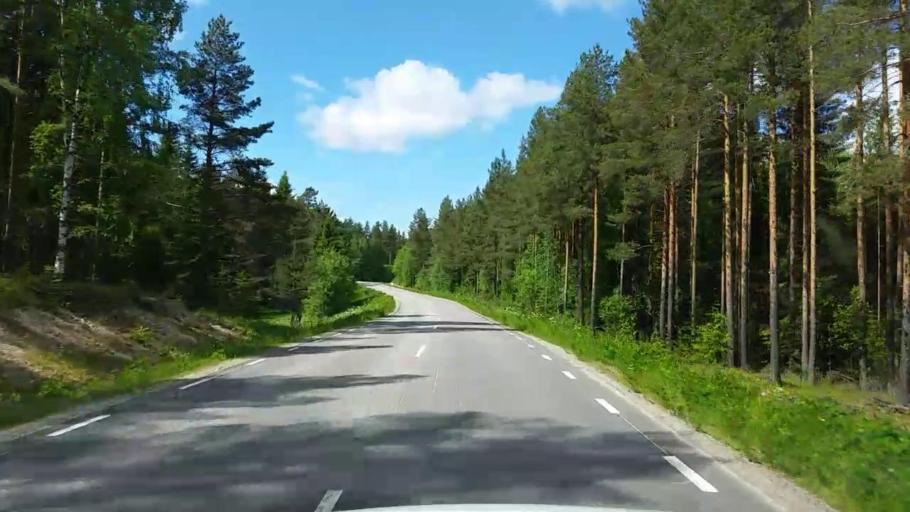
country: SE
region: Gaevleborg
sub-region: Ovanakers Kommun
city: Alfta
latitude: 61.2822
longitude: 16.0994
